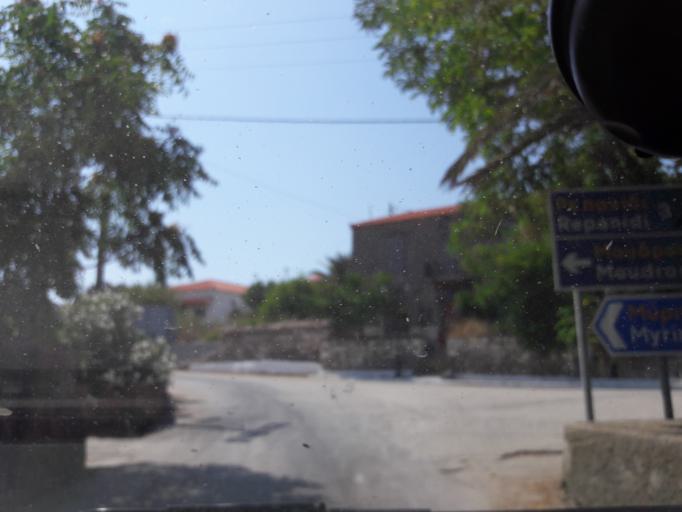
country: GR
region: North Aegean
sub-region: Nomos Lesvou
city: Myrina
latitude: 39.9047
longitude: 25.2883
